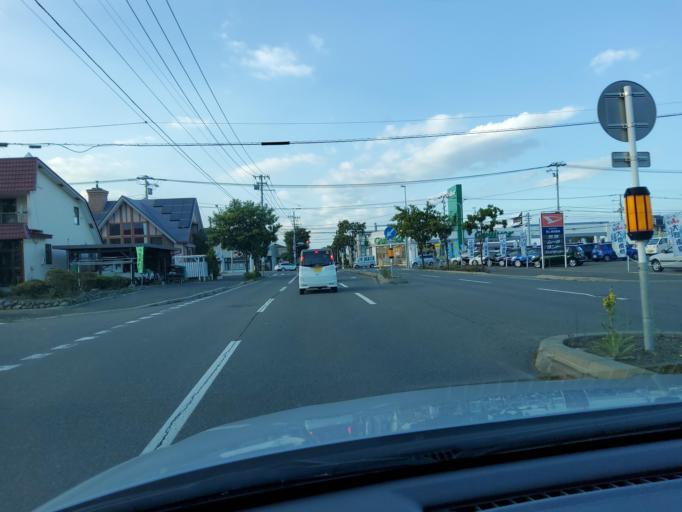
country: JP
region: Hokkaido
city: Obihiro
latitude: 42.9299
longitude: 143.1851
